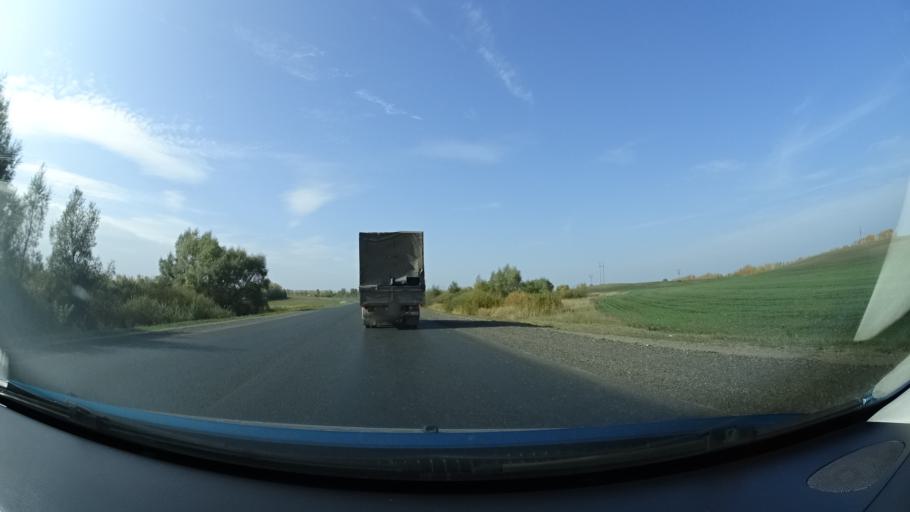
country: RU
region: Bashkortostan
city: Kandry
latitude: 54.5140
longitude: 53.9733
